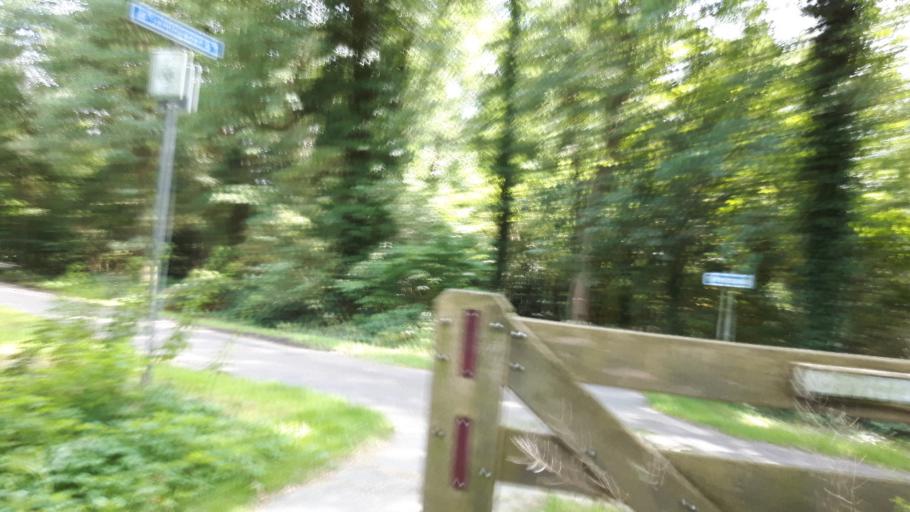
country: NL
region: Friesland
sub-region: Gemeente Heerenveen
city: Jubbega
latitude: 53.0062
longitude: 6.2907
